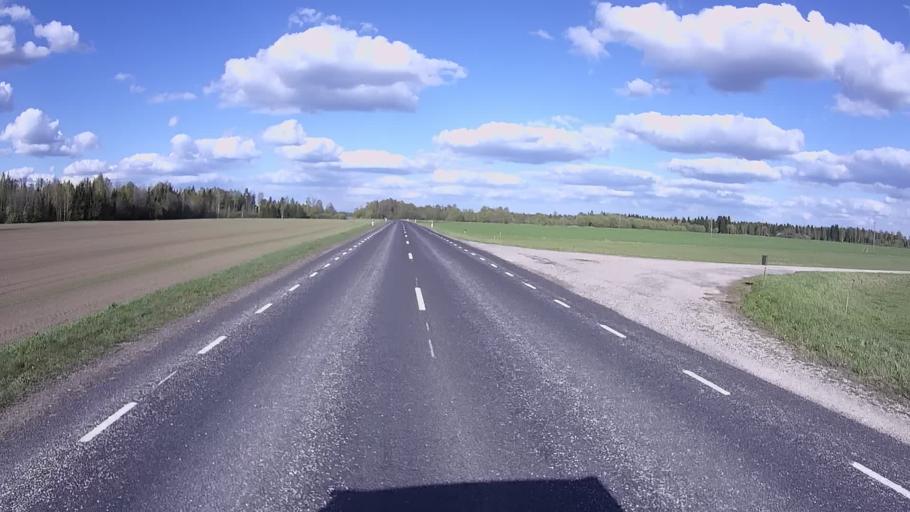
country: EE
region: Jogevamaa
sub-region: Poltsamaa linn
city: Poltsamaa
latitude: 58.7096
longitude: 26.1694
